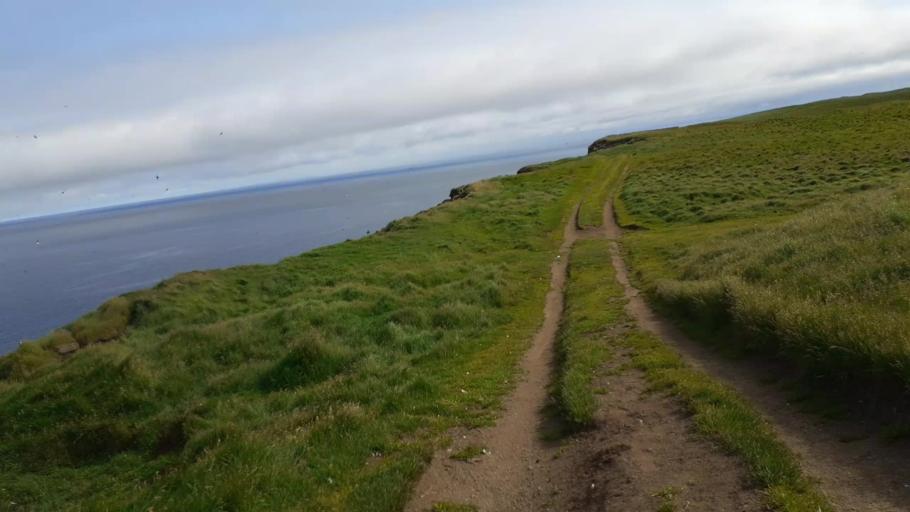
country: IS
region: Northeast
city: Dalvik
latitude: 66.5532
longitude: -17.9987
